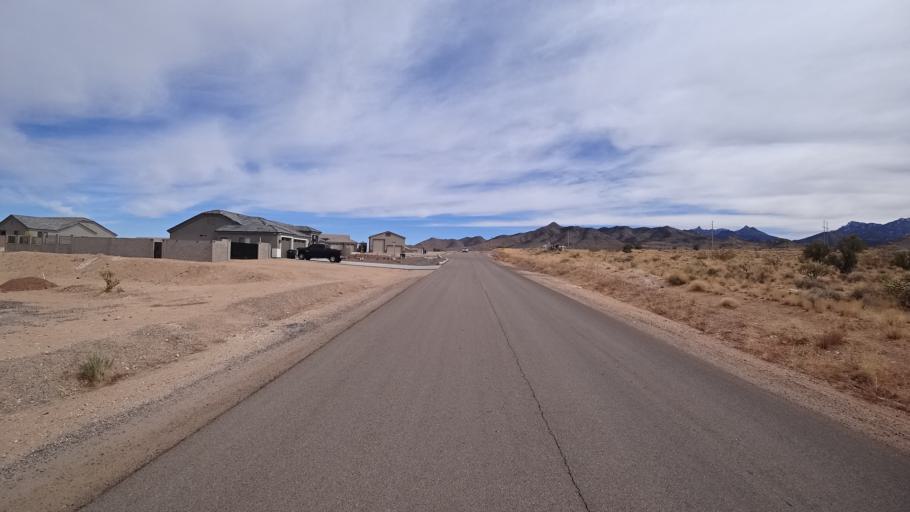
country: US
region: Arizona
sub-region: Mohave County
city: Kingman
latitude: 35.1813
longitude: -113.9789
